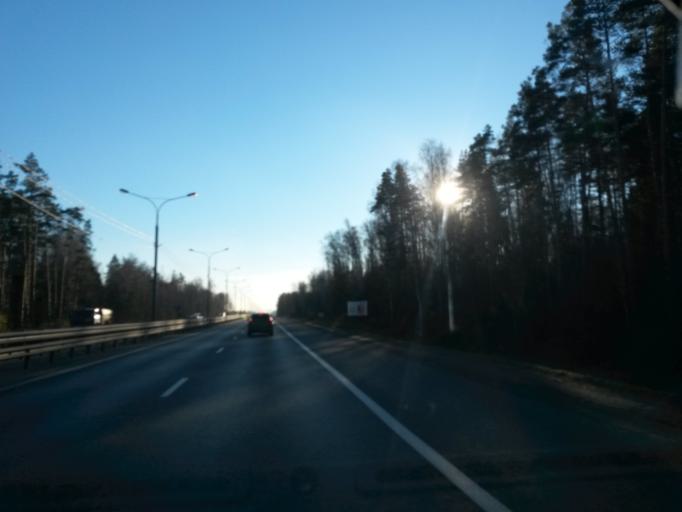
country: RU
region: Moskovskaya
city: Pushkino
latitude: 56.0334
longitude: 37.8886
